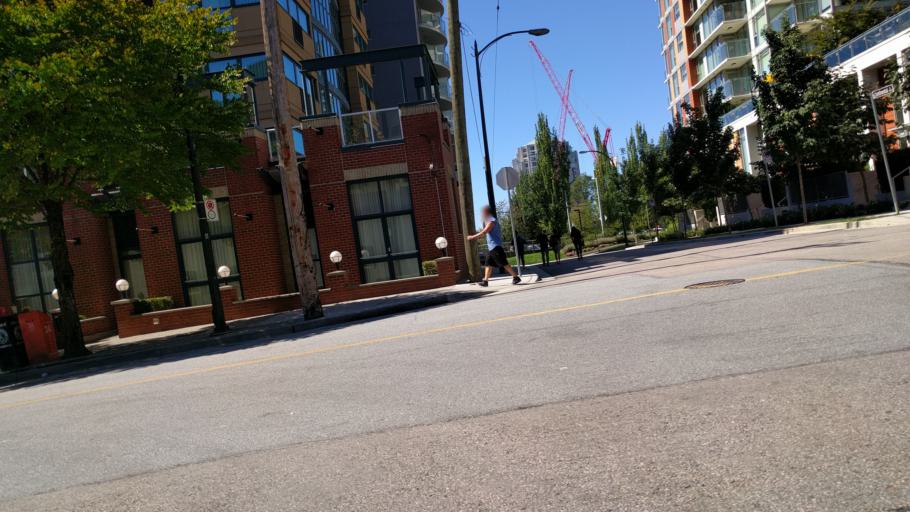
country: CA
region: British Columbia
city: West End
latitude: 49.2765
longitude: -123.1288
